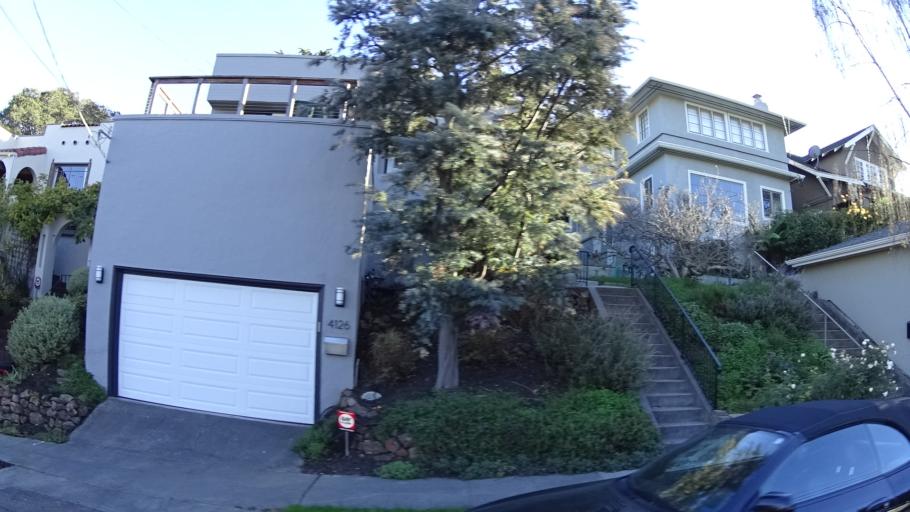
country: US
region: California
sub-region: Alameda County
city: Piedmont
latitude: 37.8073
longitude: -122.2247
